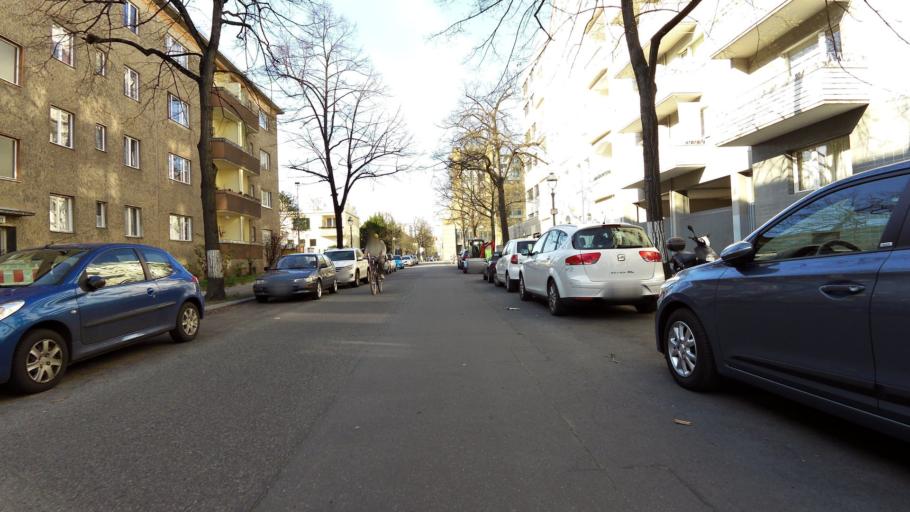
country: DE
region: Berlin
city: Wilmersdorf Bezirk
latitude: 52.4857
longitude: 13.3157
